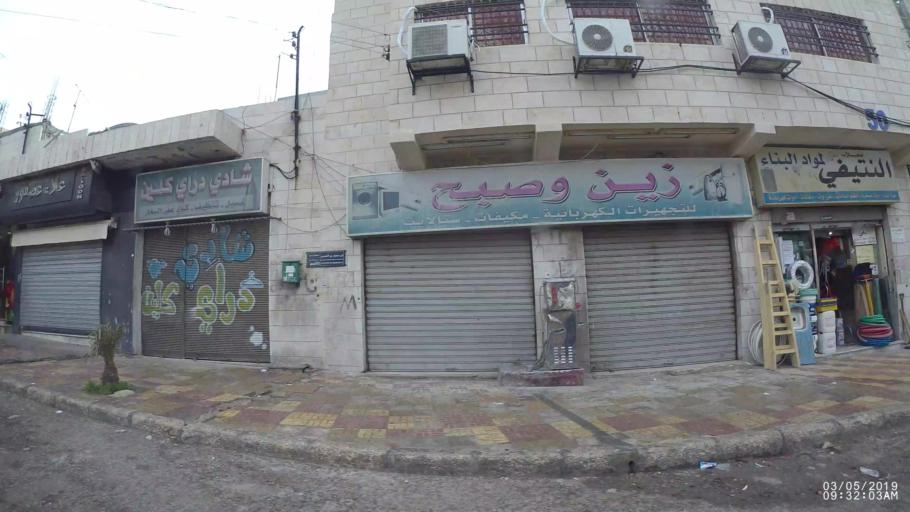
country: JO
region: Amman
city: Amman
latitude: 31.9769
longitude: 35.9246
